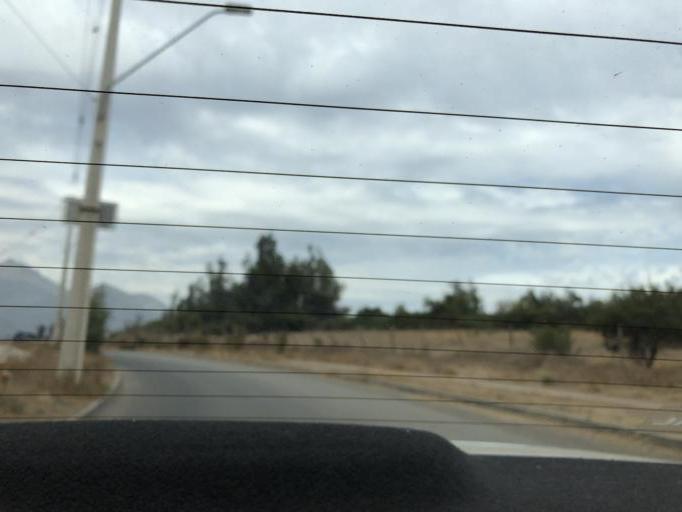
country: CL
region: Santiago Metropolitan
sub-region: Provincia de Cordillera
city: Puente Alto
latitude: -33.5901
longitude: -70.5204
